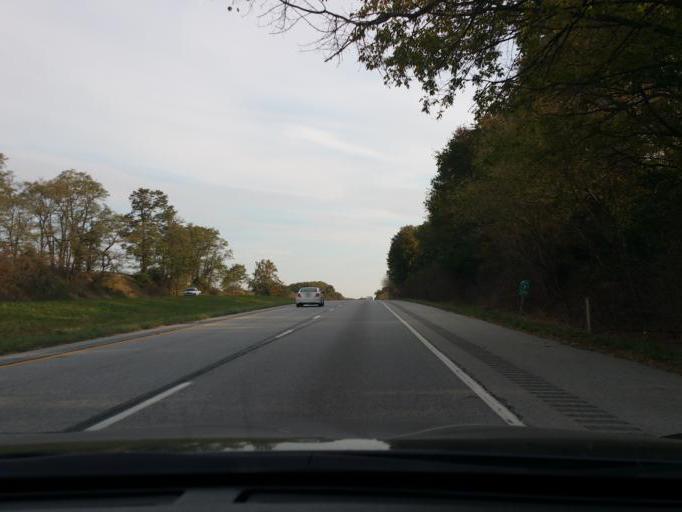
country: US
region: Pennsylvania
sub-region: Chester County
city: Oxford
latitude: 39.7690
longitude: -76.0121
